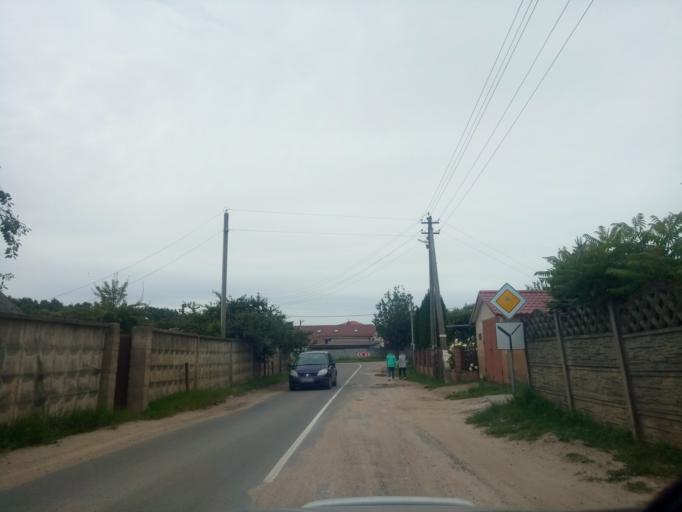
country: BY
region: Minsk
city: Zhdanovichy
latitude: 53.9250
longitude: 27.3839
